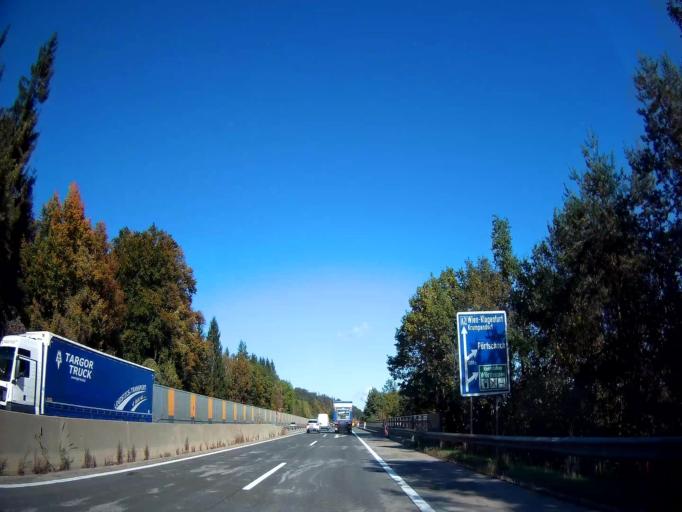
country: AT
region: Carinthia
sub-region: Politischer Bezirk Klagenfurt Land
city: Schiefling am See
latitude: 46.6281
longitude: 14.0881
